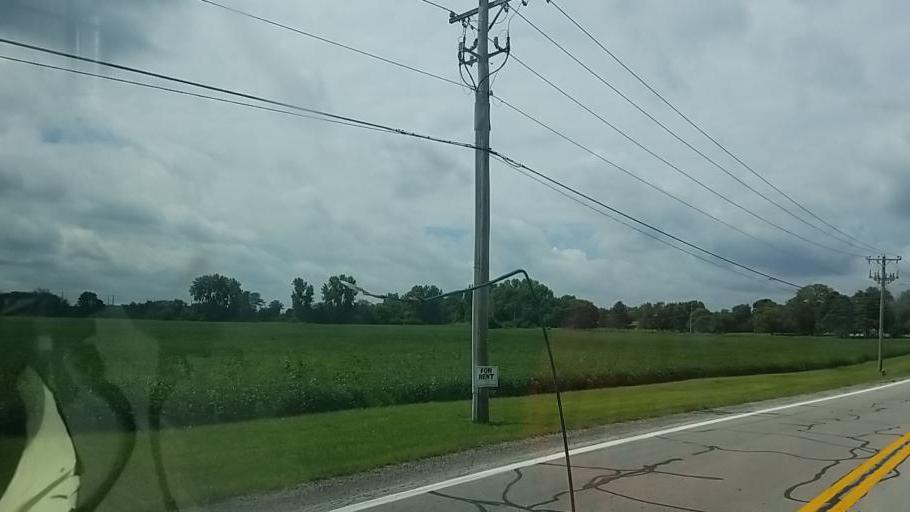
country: US
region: Ohio
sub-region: Fayette County
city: Jeffersonville
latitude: 39.6512
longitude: -83.5500
